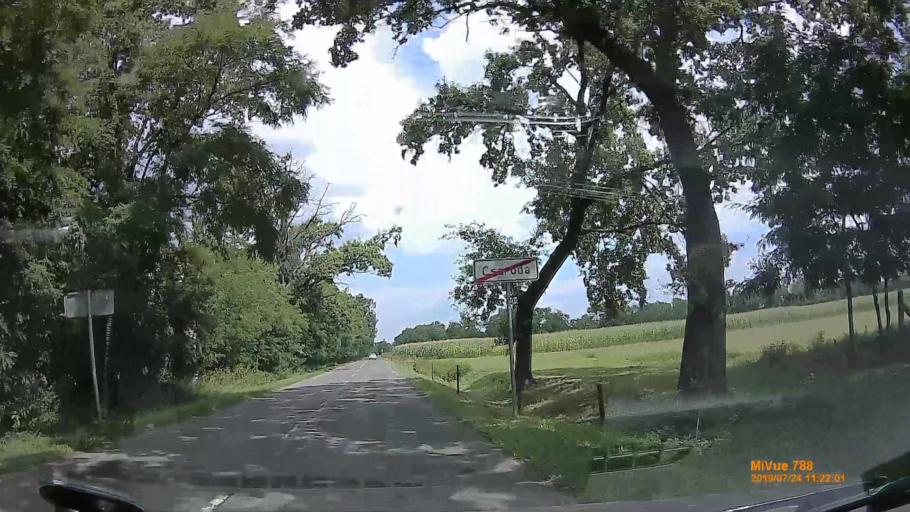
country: HU
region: Szabolcs-Szatmar-Bereg
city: Tarpa
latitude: 48.1712
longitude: 22.4610
